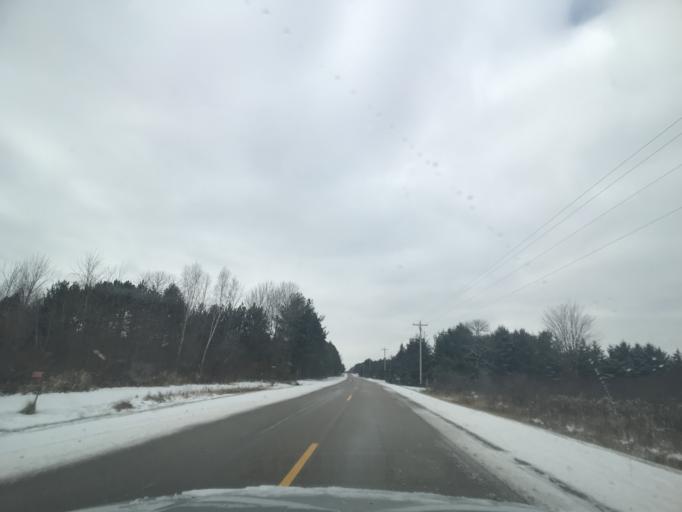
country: US
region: Wisconsin
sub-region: Brown County
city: Suamico
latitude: 44.7061
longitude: -88.0854
